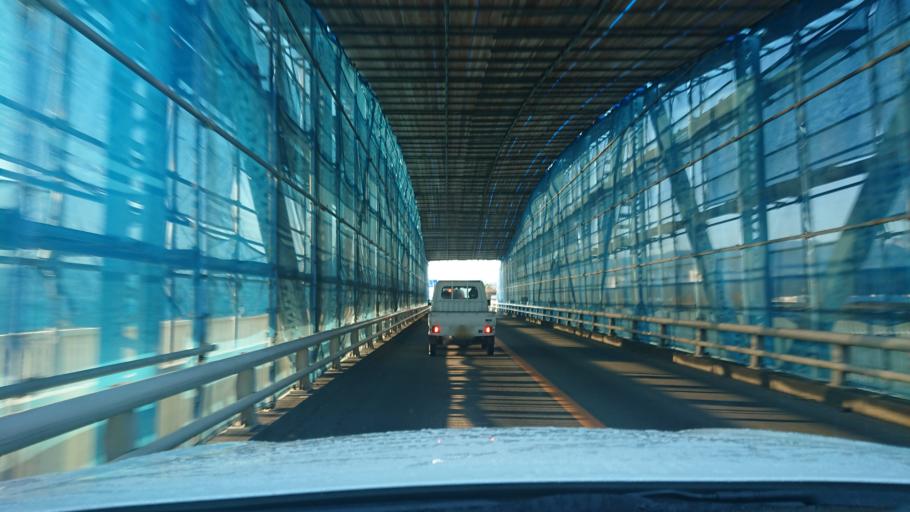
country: JP
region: Tokushima
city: Anan
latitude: 33.9393
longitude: 134.6218
